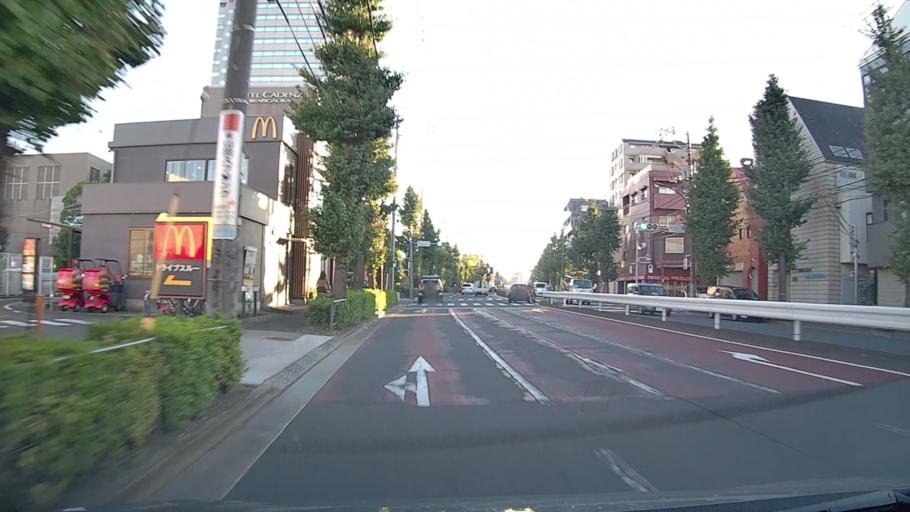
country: JP
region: Saitama
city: Wako
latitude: 35.7570
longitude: 139.6208
